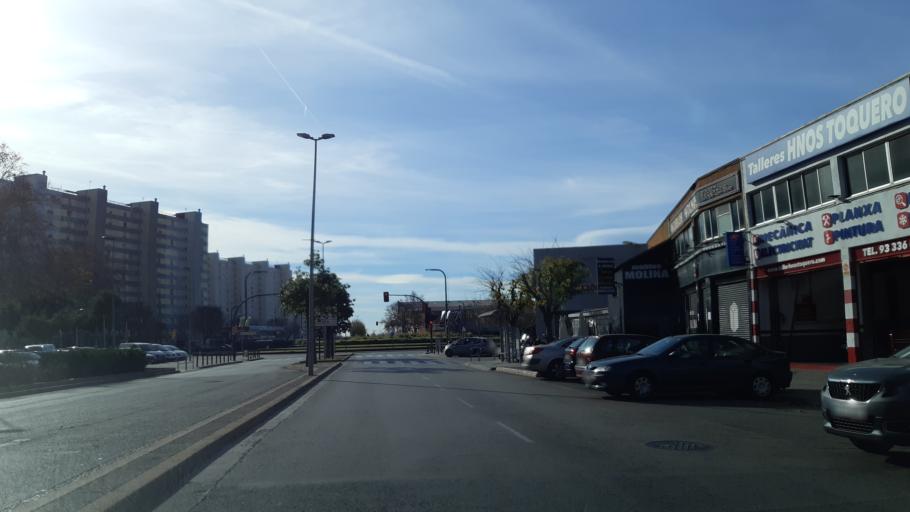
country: ES
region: Catalonia
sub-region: Provincia de Barcelona
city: L'Hospitalet de Llobregat
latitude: 41.3539
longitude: 2.1081
